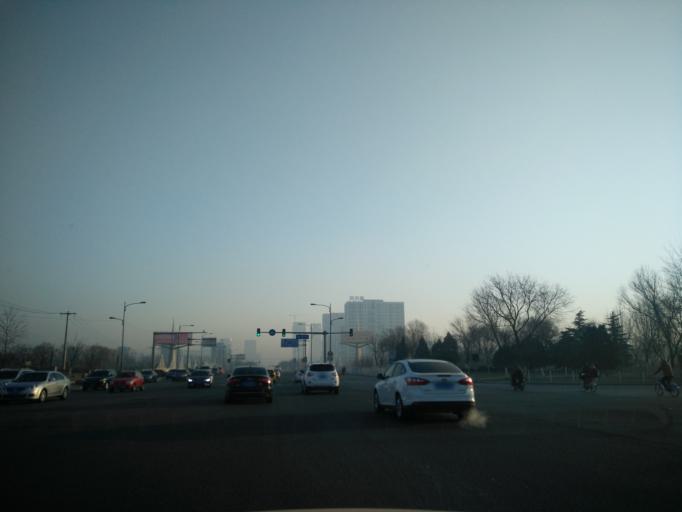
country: CN
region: Beijing
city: Jiugong
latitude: 39.7817
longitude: 116.4835
